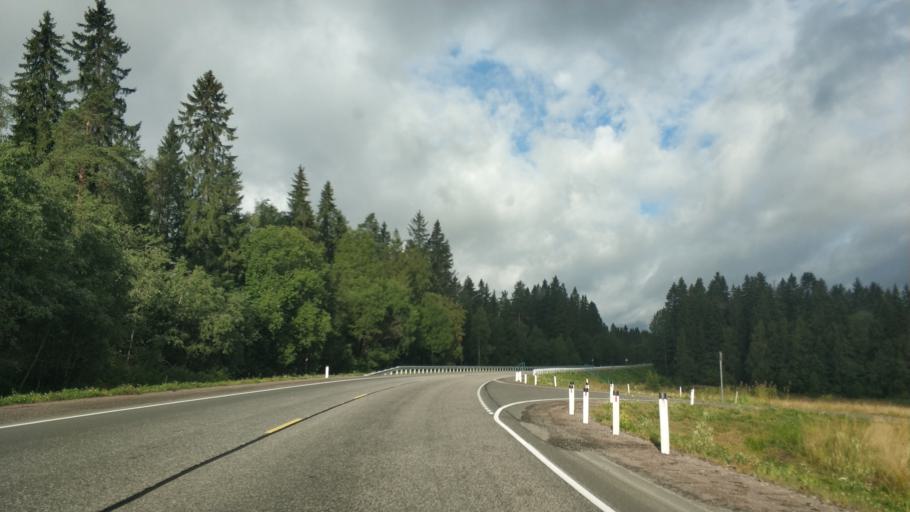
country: RU
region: Republic of Karelia
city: Khelyulya
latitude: 61.7851
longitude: 30.6442
